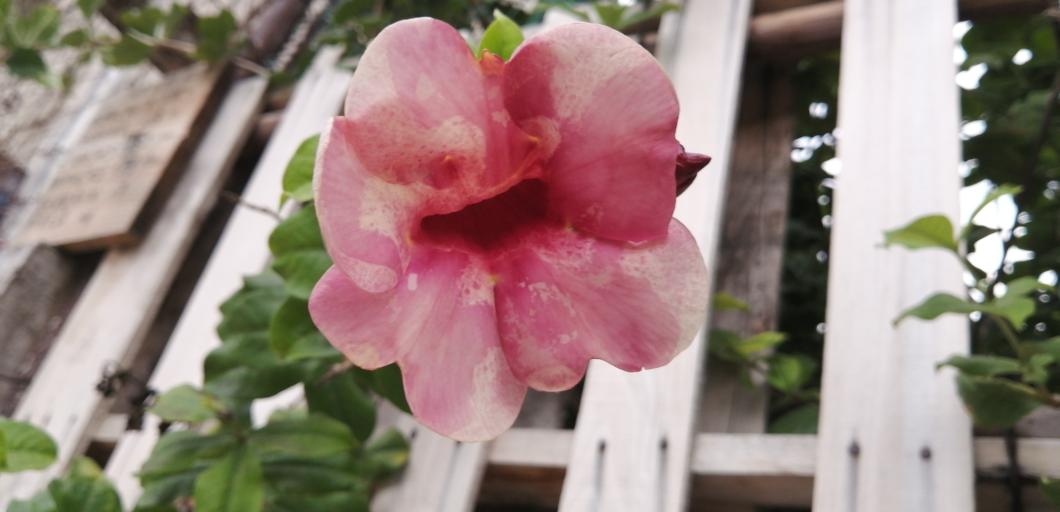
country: MX
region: Quintana Roo
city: Playa del Carmen
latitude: 20.6406
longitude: -87.0622
